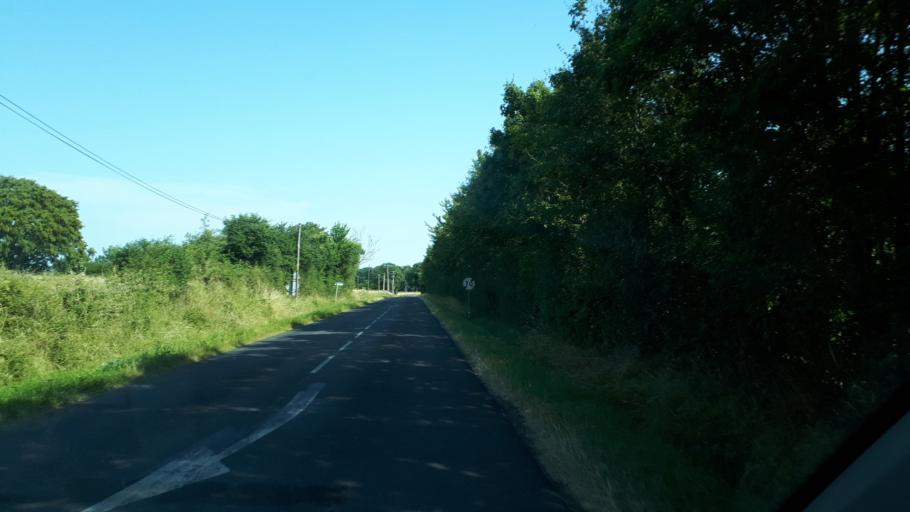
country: FR
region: Centre
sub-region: Departement du Loir-et-Cher
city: Droue
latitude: 47.9854
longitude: 1.0388
